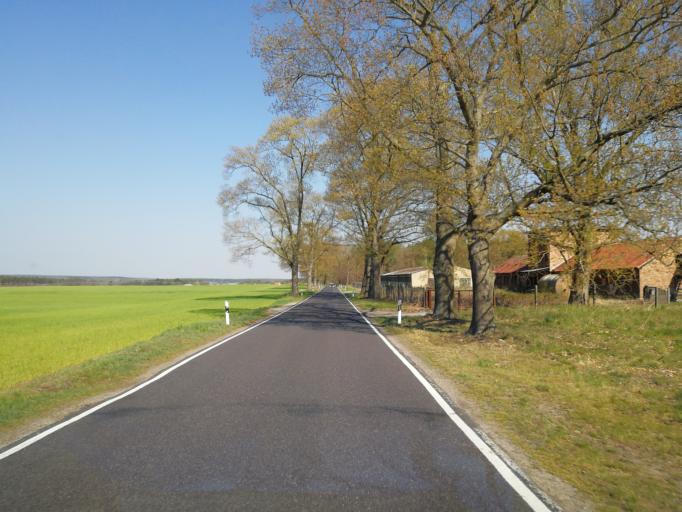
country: DE
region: Brandenburg
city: Bronkow
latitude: 51.7164
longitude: 13.8635
